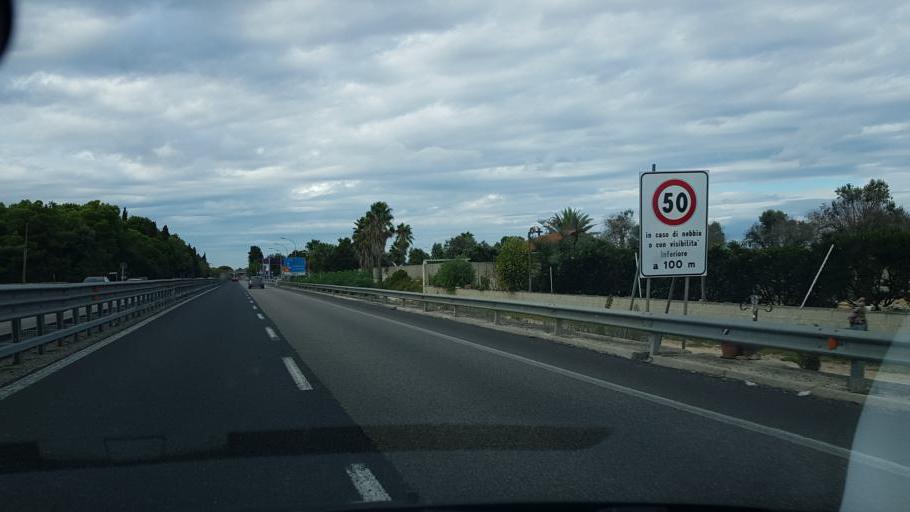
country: IT
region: Apulia
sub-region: Provincia di Lecce
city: Cavallino
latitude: 40.3024
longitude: 18.1927
